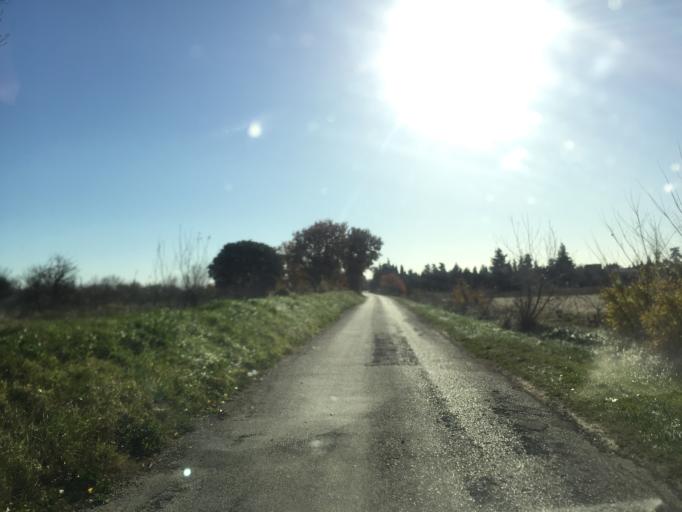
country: FR
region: Provence-Alpes-Cote d'Azur
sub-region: Departement du Vaucluse
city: Jonquieres
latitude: 44.0990
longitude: 4.9165
